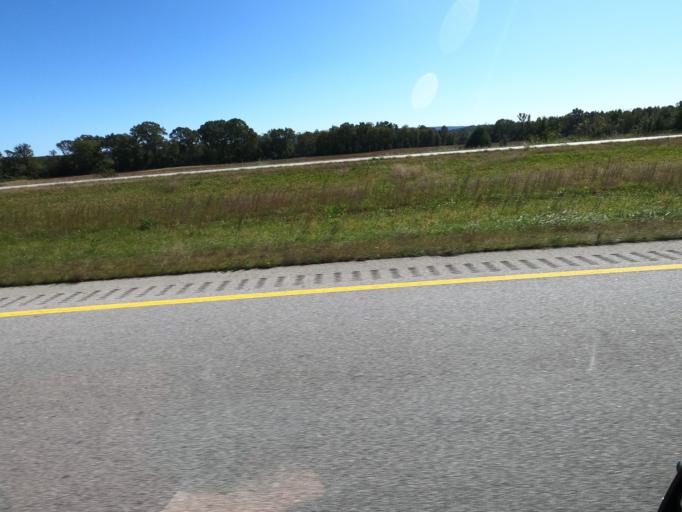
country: US
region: Tennessee
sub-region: Marion County
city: Kimball
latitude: 35.0415
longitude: -85.6789
